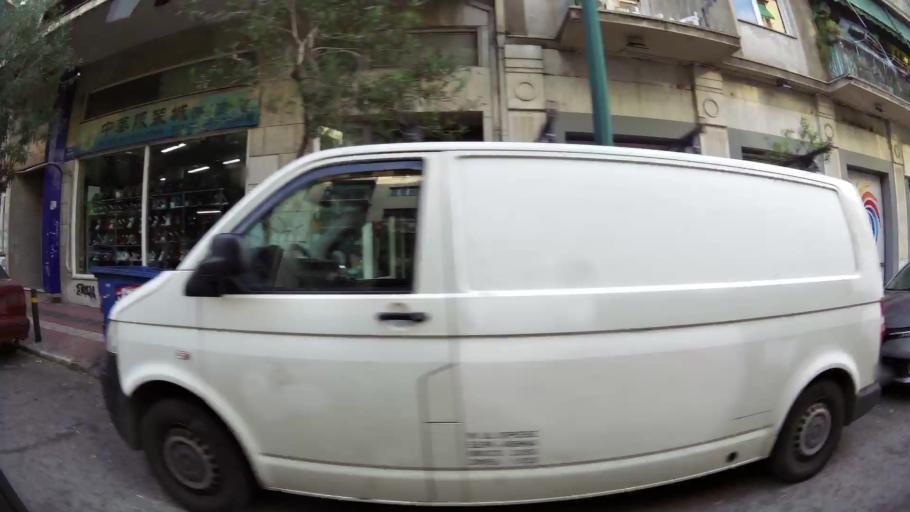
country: GR
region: Attica
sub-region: Nomarchia Athinas
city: Kipseli
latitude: 37.9955
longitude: 23.7272
